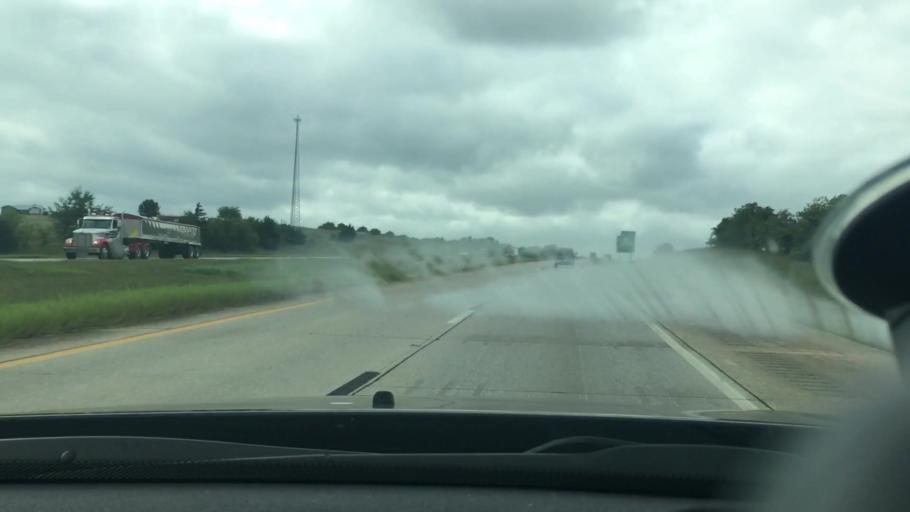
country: US
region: Oklahoma
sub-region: Bryan County
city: Durant
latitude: 34.1443
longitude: -96.2664
